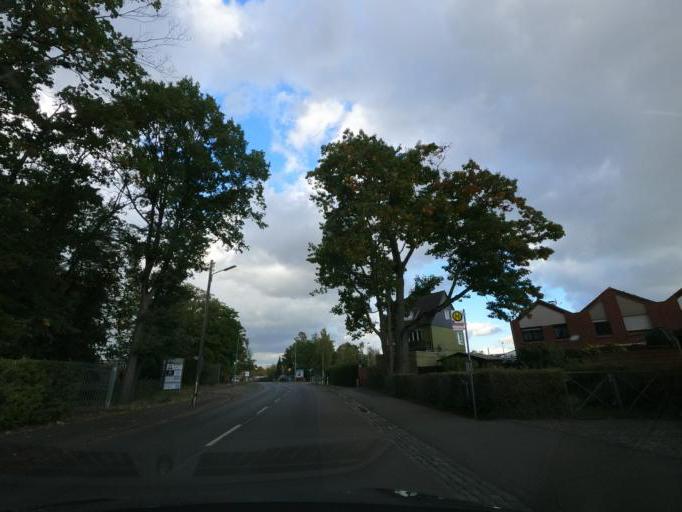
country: DE
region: Lower Saxony
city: Braunschweig
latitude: 52.2846
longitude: 10.5638
